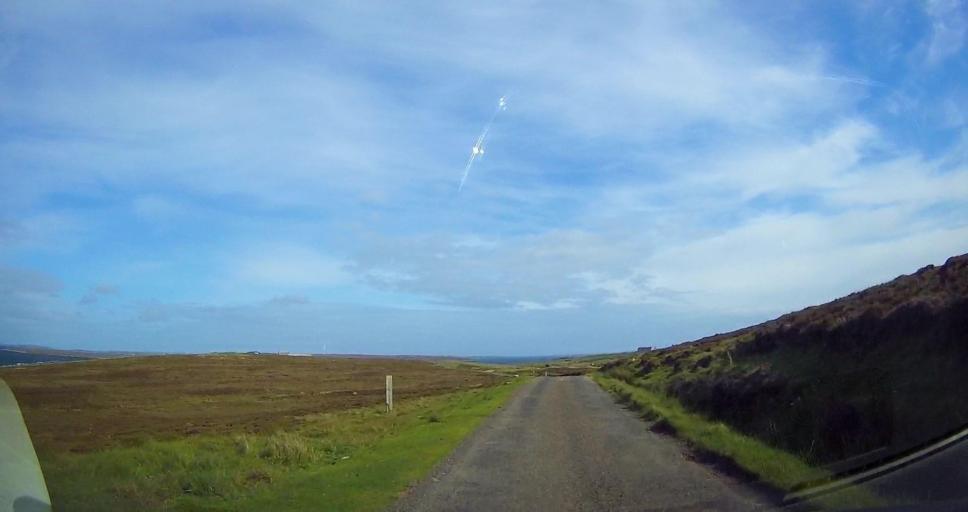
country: GB
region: Scotland
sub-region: Orkney Islands
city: Stromness
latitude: 58.8558
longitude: -3.2125
